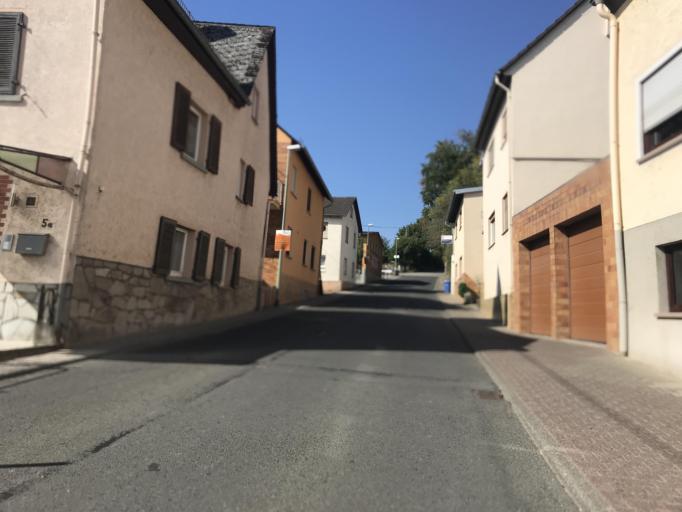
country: DE
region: Hesse
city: Geisenheim
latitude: 50.0349
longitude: 7.9466
